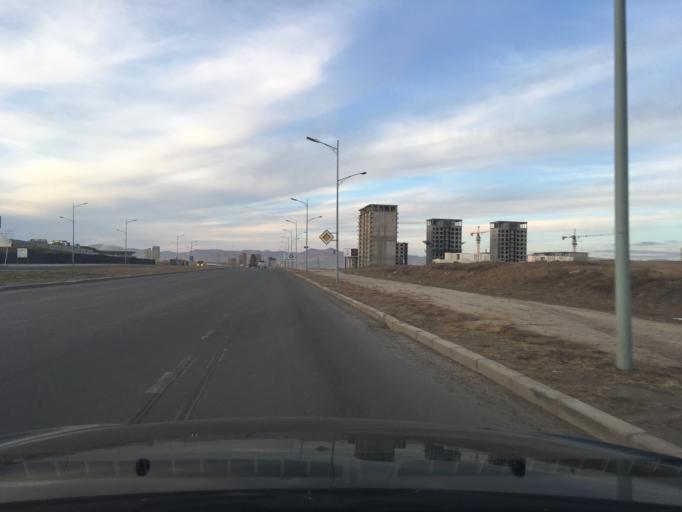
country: MN
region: Ulaanbaatar
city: Ulaanbaatar
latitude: 47.8451
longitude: 106.7909
